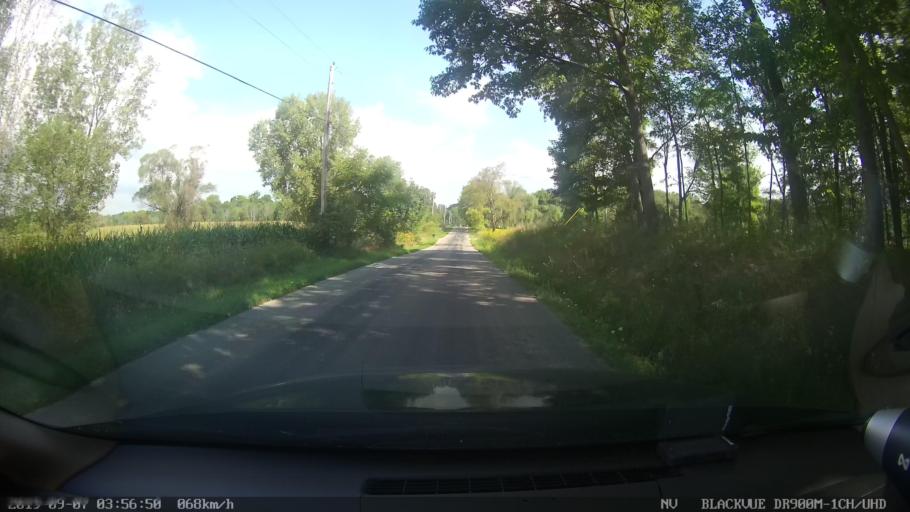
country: US
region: Ohio
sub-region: Licking County
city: Granville
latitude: 40.1738
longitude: -82.5630
